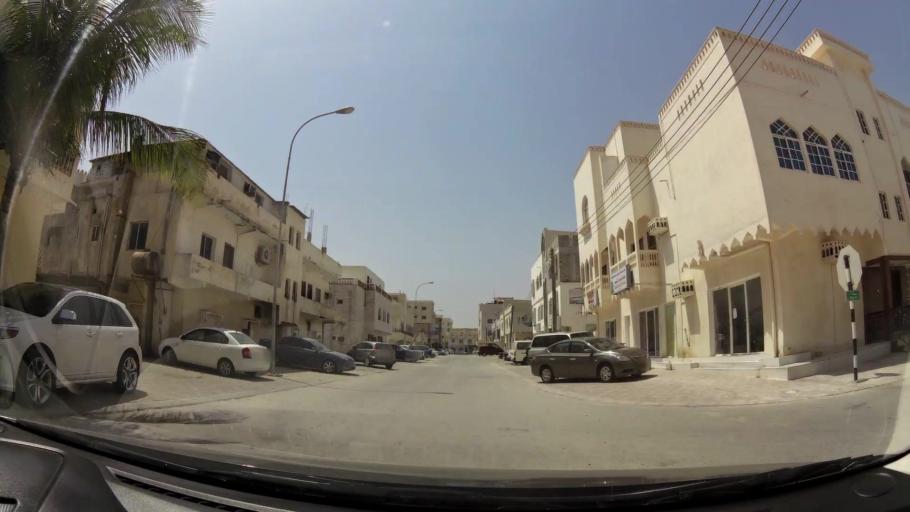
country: OM
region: Zufar
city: Salalah
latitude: 17.0158
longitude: 54.0856
